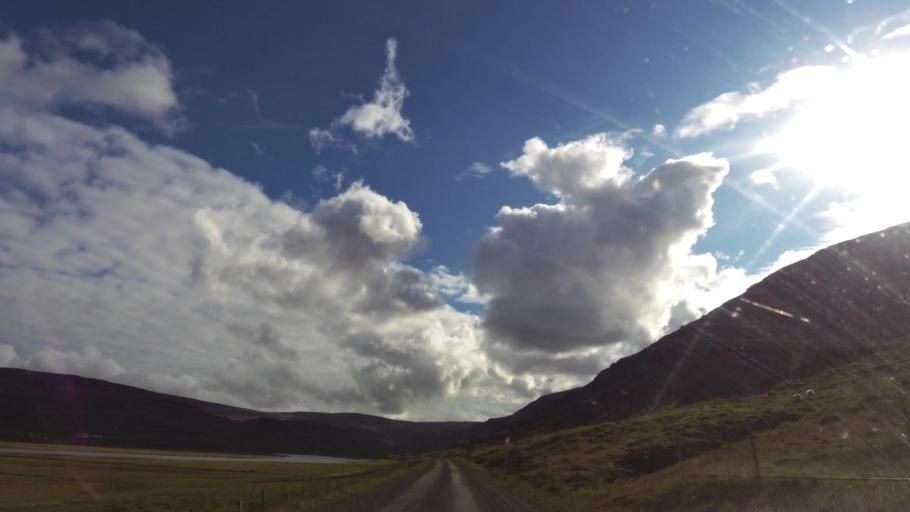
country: IS
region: West
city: Olafsvik
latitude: 65.5761
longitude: -24.1525
